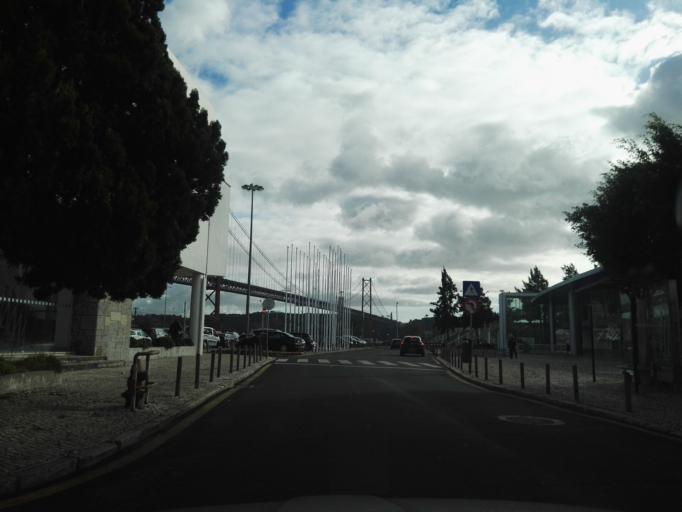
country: PT
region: Setubal
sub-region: Almada
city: Pragal
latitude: 38.6995
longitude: -9.1835
